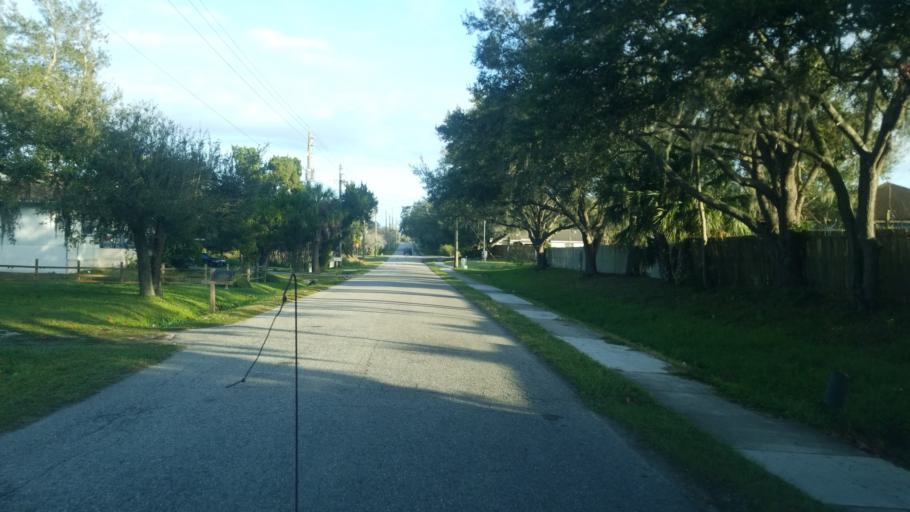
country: US
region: Florida
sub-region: Manatee County
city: Samoset
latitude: 27.4423
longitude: -82.5342
